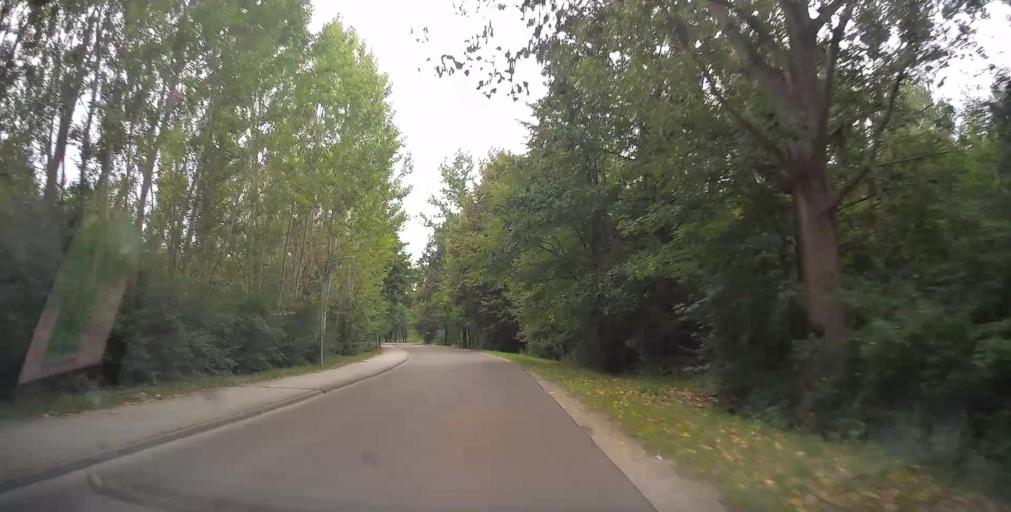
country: PL
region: Masovian Voivodeship
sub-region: Powiat bialobrzeski
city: Sucha
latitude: 51.6330
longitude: 20.9538
